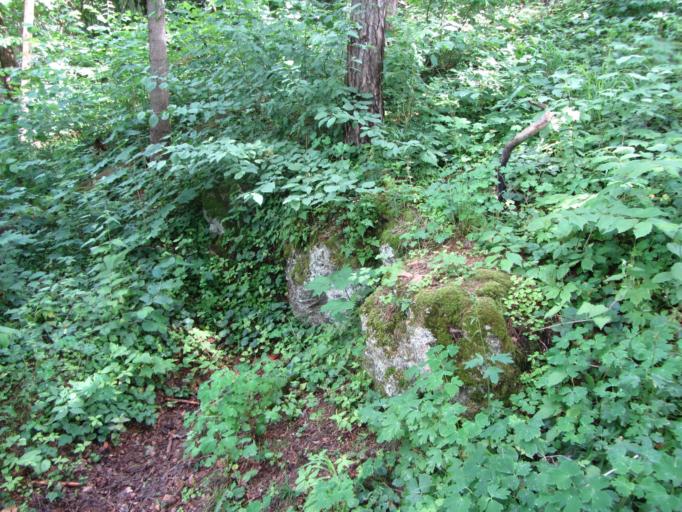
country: LT
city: Grigiskes
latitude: 54.7418
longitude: 25.0247
